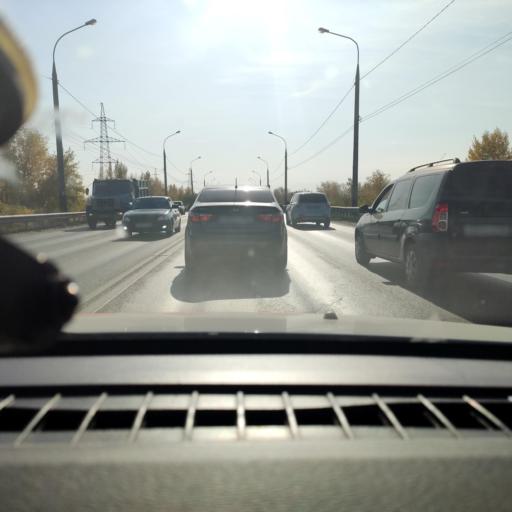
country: RU
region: Samara
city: Samara
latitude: 53.1621
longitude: 50.1945
